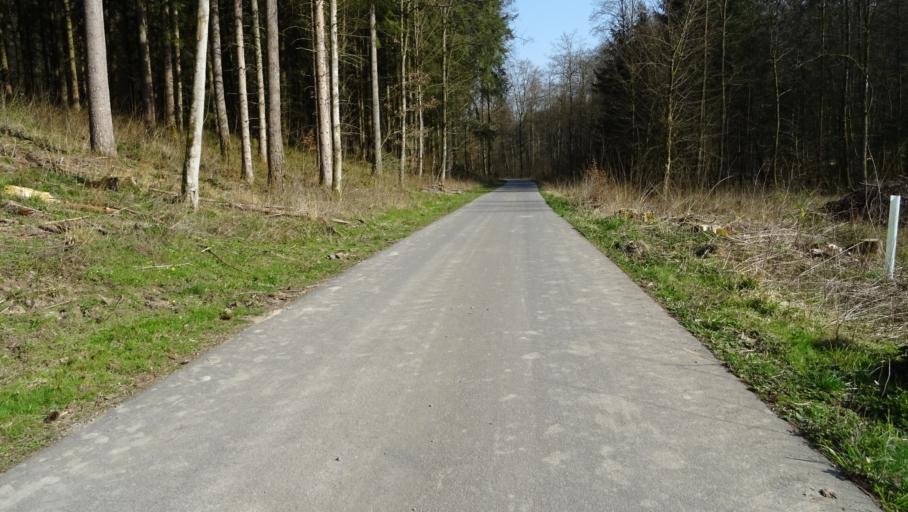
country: DE
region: Baden-Wuerttemberg
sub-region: Regierungsbezirk Stuttgart
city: Roigheim
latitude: 49.3882
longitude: 9.3366
